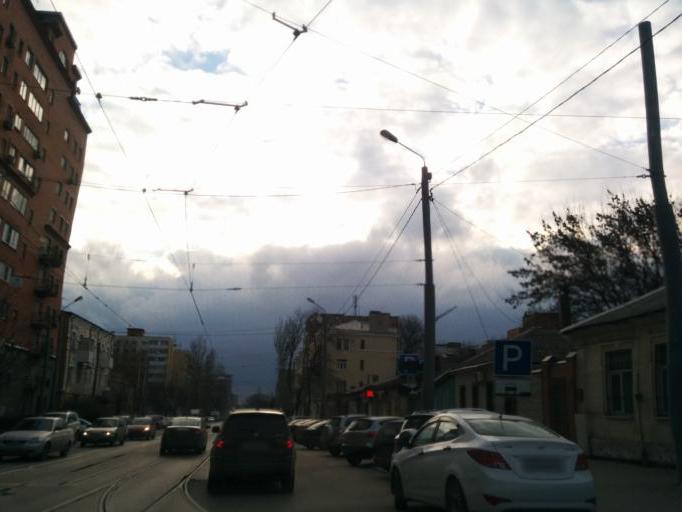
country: RU
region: Rostov
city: Rostov-na-Donu
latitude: 47.2309
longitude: 39.7345
